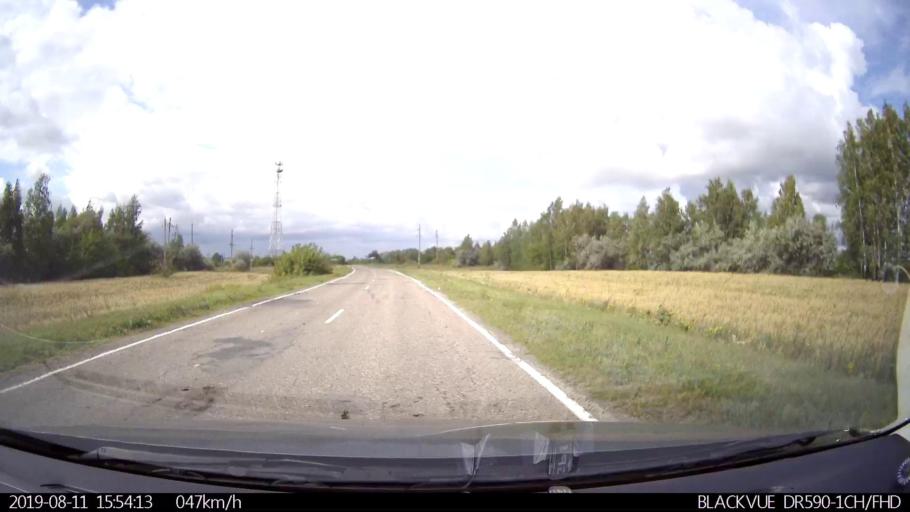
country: RU
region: Ulyanovsk
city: Ignatovka
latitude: 53.9398
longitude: 47.6567
